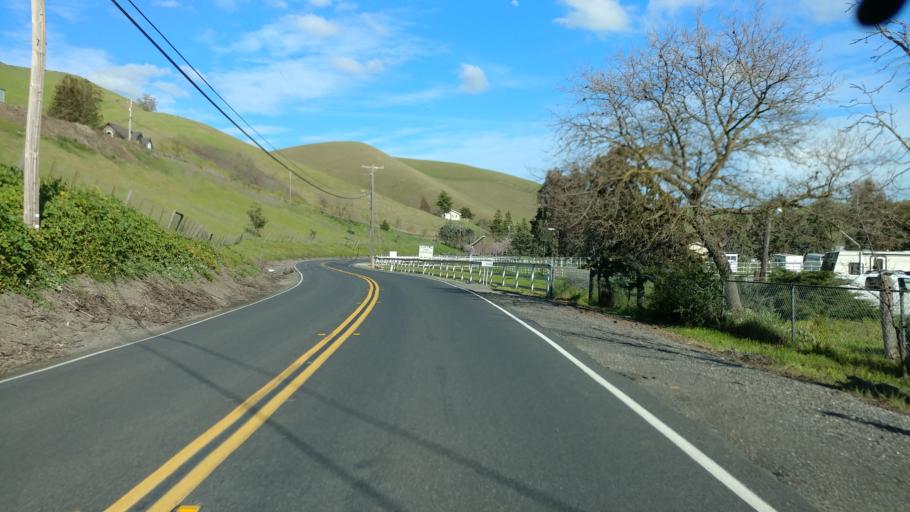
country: US
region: California
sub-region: Contra Costa County
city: Blackhawk
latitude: 37.7761
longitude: -121.8590
